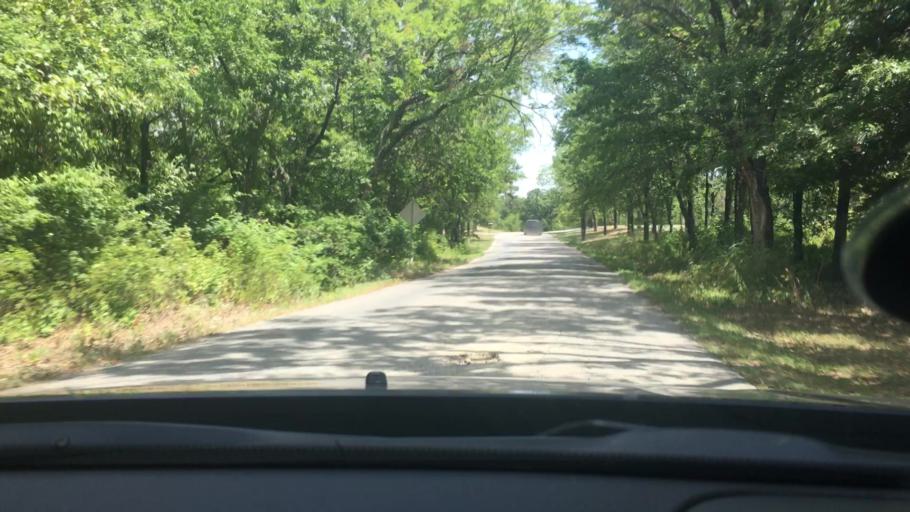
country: US
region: Oklahoma
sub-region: Carter County
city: Ardmore
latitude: 34.0717
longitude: -97.1860
